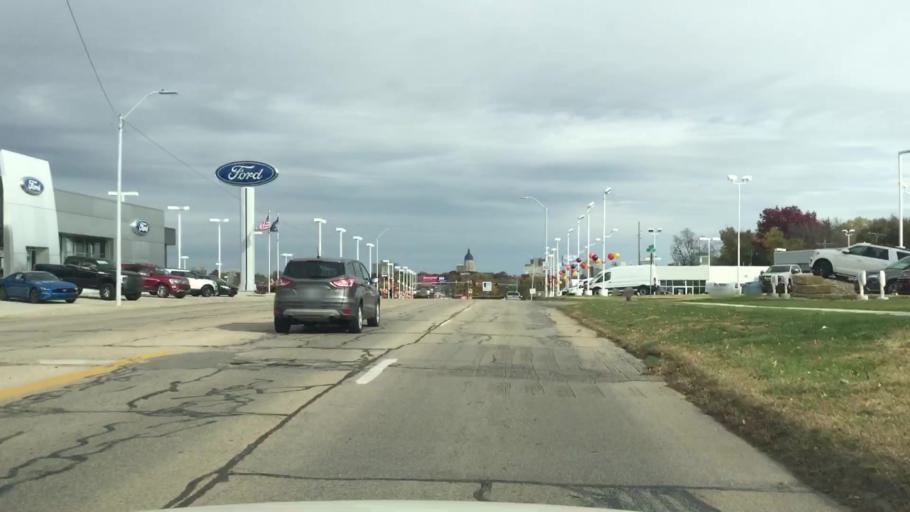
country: US
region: Kansas
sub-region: Shawnee County
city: Topeka
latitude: 39.0275
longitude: -95.6836
